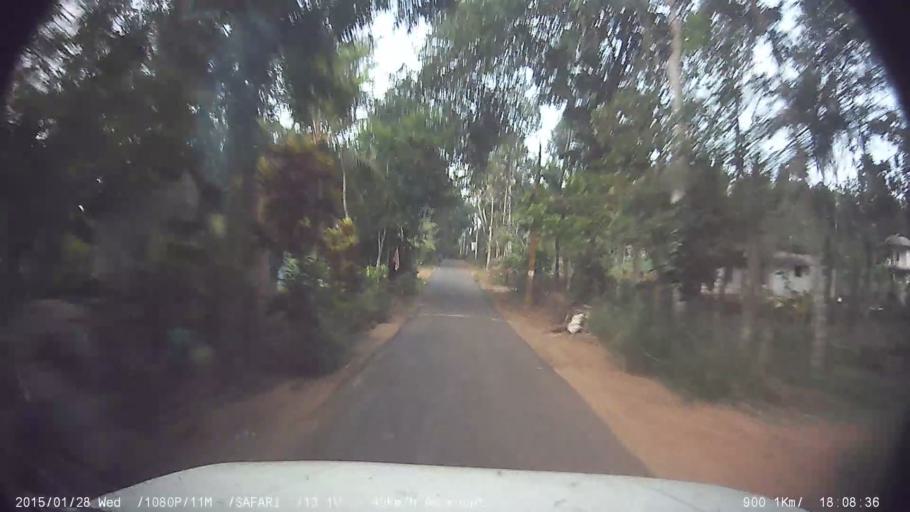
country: IN
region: Kerala
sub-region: Kottayam
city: Palackattumala
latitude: 9.7417
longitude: 76.5751
